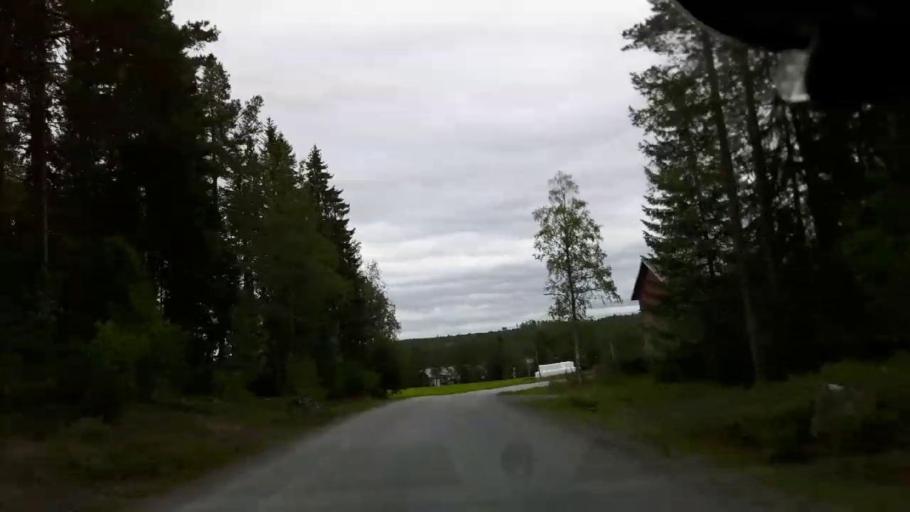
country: SE
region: Jaemtland
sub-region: OEstersunds Kommun
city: Brunflo
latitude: 63.1010
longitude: 15.1051
